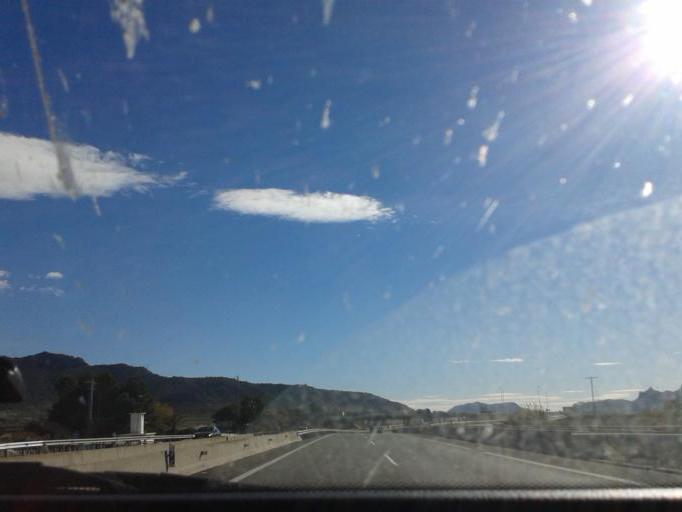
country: ES
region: Valencia
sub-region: Provincia de Alicante
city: Villena
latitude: 38.6118
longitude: -0.8493
